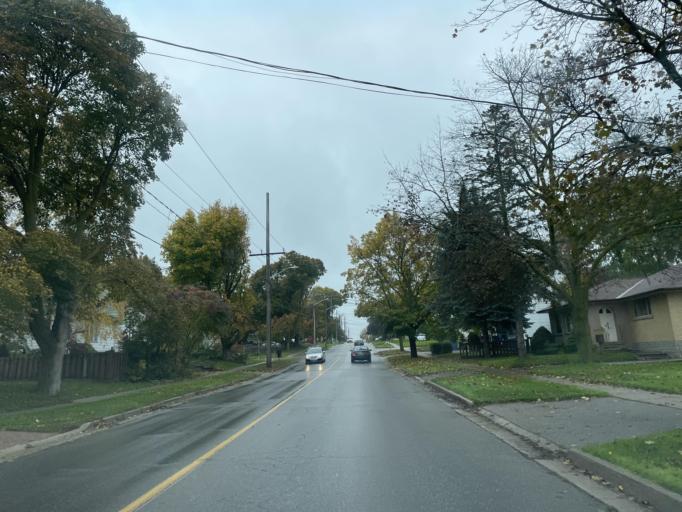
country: CA
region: Ontario
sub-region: Wellington County
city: Guelph
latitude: 43.5347
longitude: -80.2713
